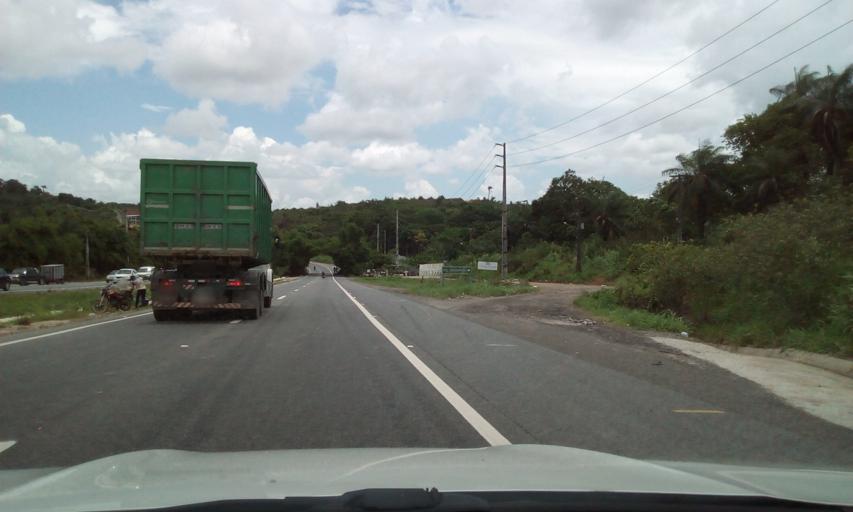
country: BR
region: Pernambuco
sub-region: Paulista
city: Paulista
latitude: -7.9758
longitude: -34.9235
